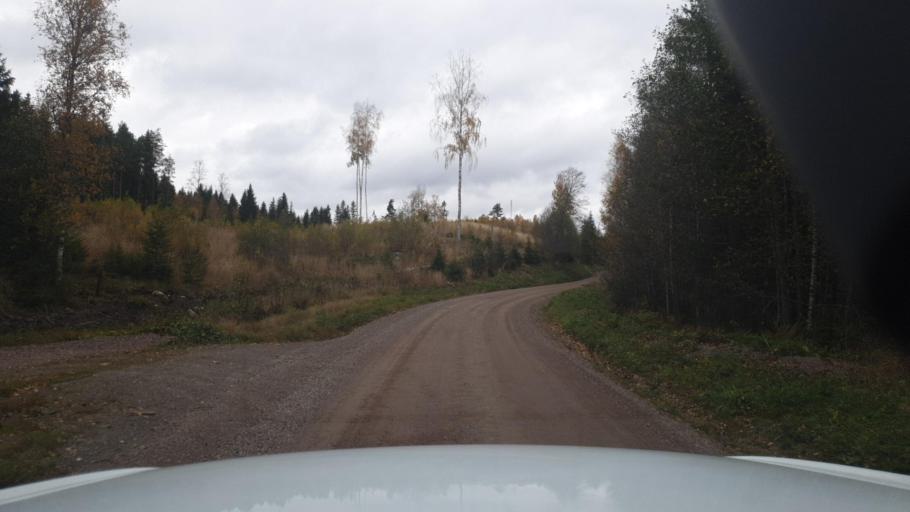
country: SE
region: Vaermland
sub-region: Arvika Kommun
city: Arvika
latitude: 59.9494
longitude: 12.6605
